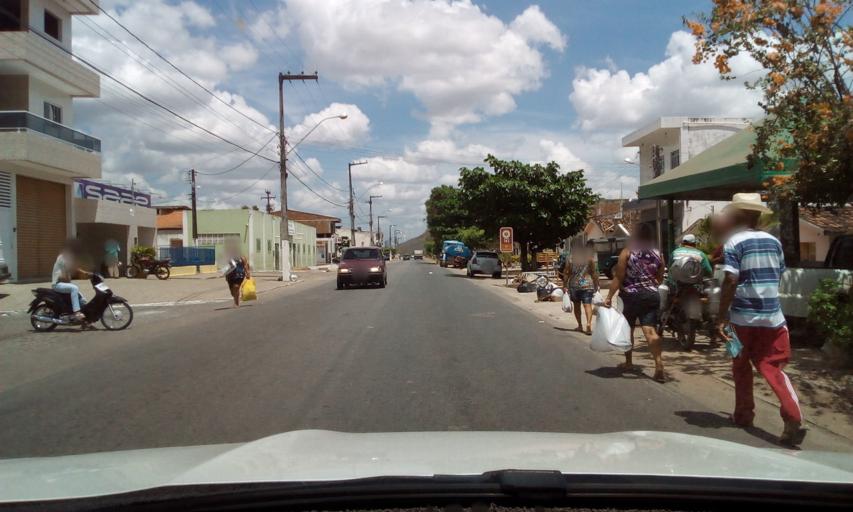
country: BR
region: Paraiba
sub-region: Alagoinha
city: Alagoinha
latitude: -6.9486
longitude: -35.5445
